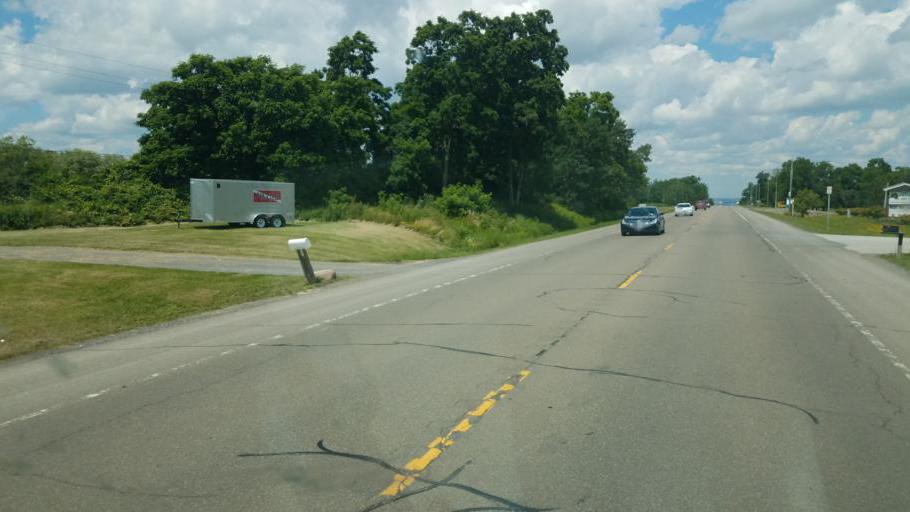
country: US
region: New York
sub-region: Yates County
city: Keuka Park
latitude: 42.5845
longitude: -77.0367
